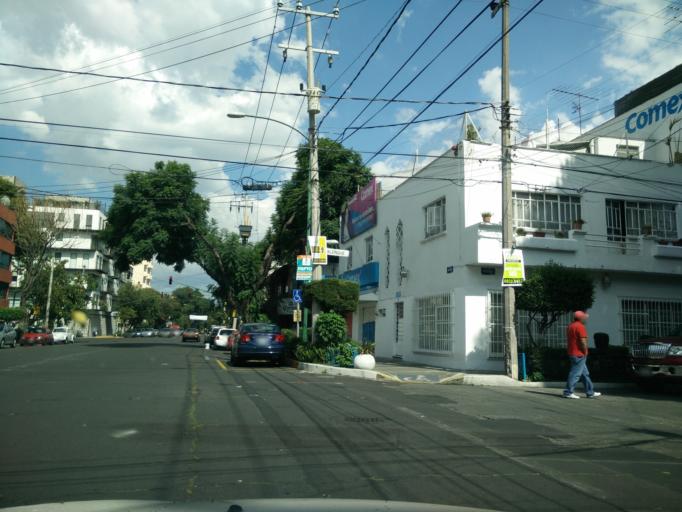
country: MX
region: Mexico City
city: Colonia del Valle
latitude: 19.3787
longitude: -99.1541
